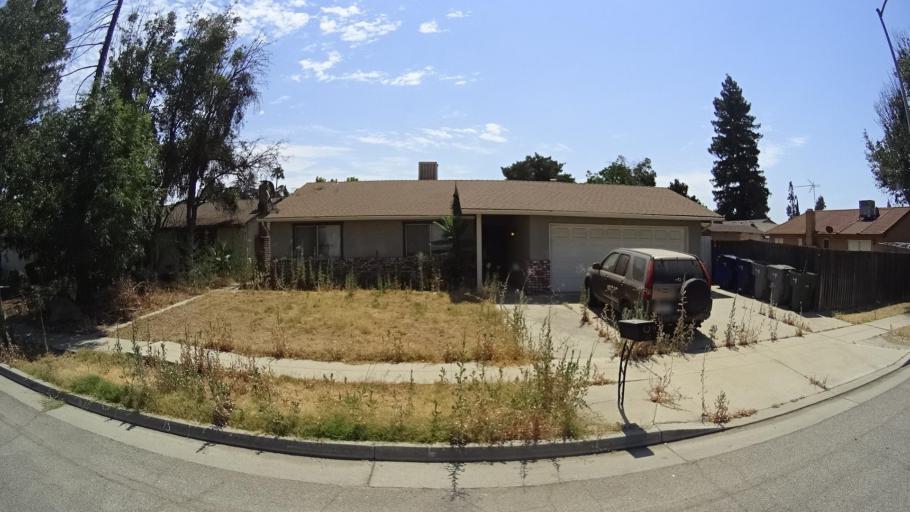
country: US
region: California
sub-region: Fresno County
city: Sunnyside
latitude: 36.7436
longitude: -119.6938
